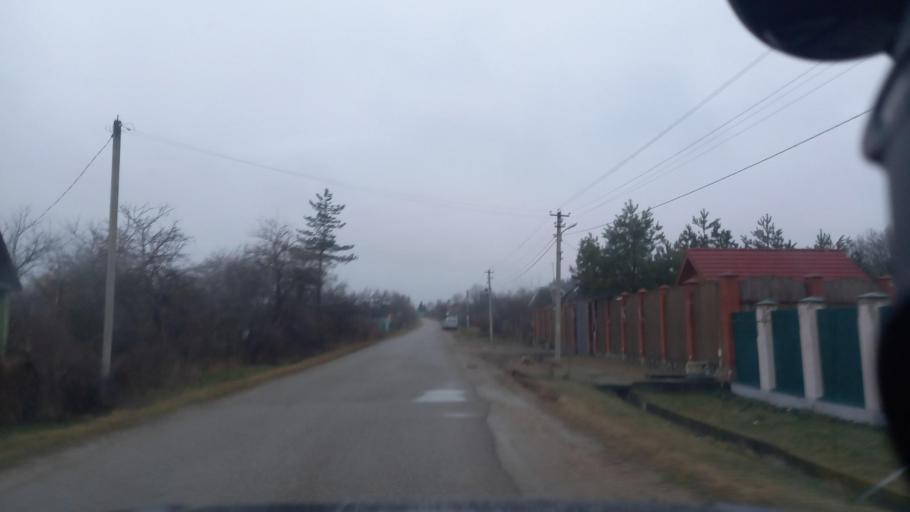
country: RU
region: Krasnodarskiy
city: Saratovskaya
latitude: 44.6483
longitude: 39.3185
